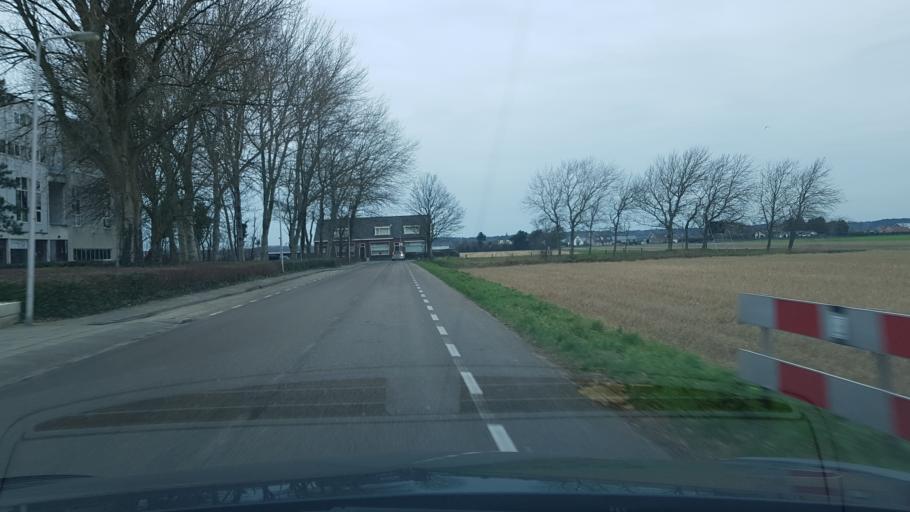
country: NL
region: South Holland
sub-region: Gemeente Noordwijkerhout
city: Noordwijkerhout
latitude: 52.2526
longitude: 4.4738
